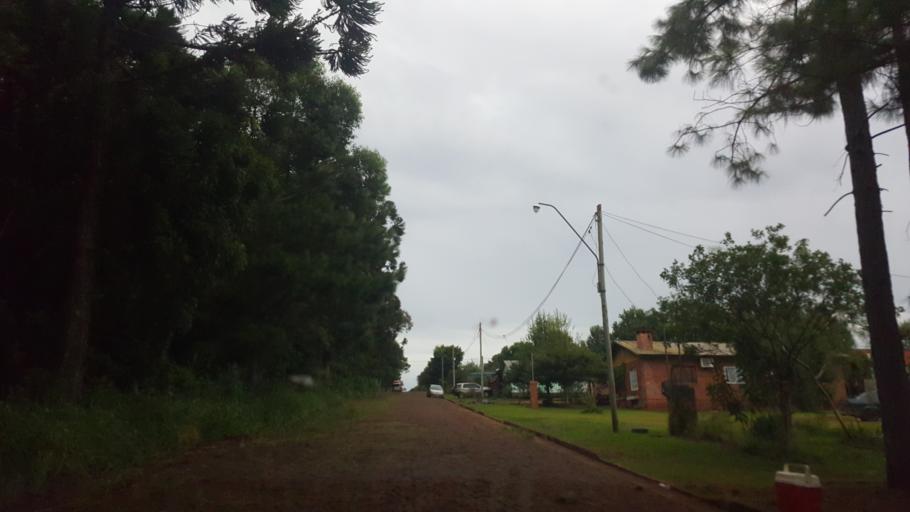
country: AR
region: Misiones
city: Capiovi
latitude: -26.9268
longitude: -55.0496
